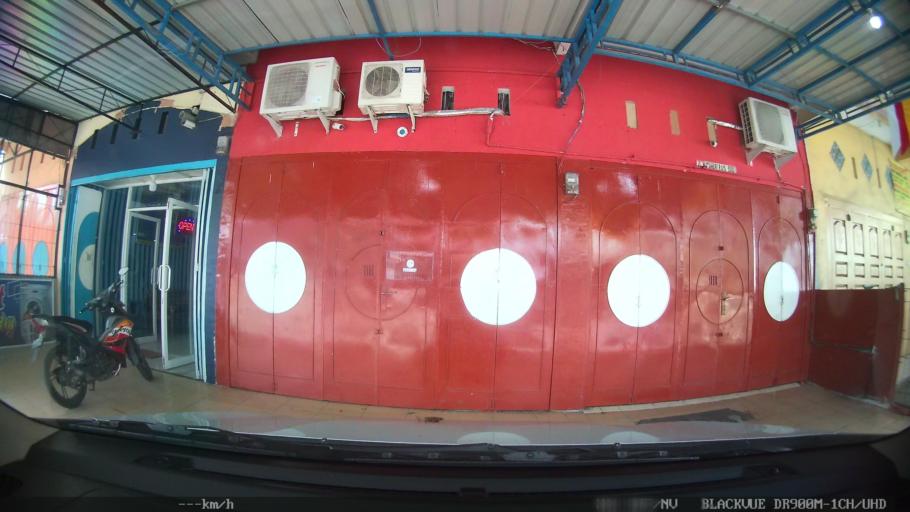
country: ID
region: North Sumatra
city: Sunggal
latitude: 3.6091
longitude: 98.6296
